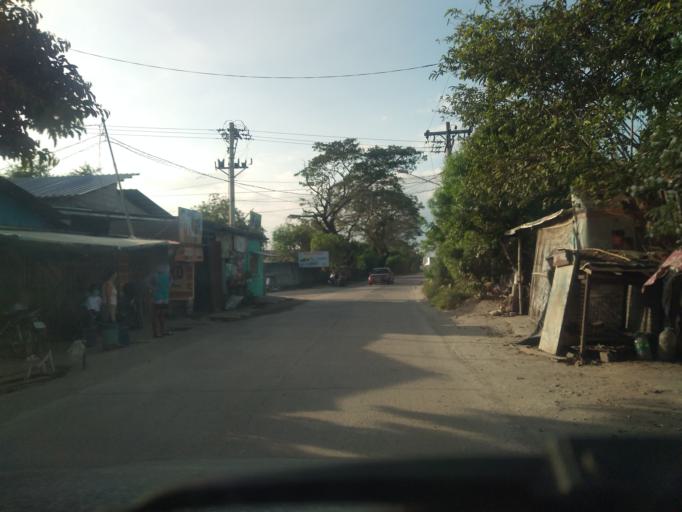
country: PH
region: Central Luzon
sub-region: Province of Pampanga
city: Malino
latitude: 15.1042
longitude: 120.6743
